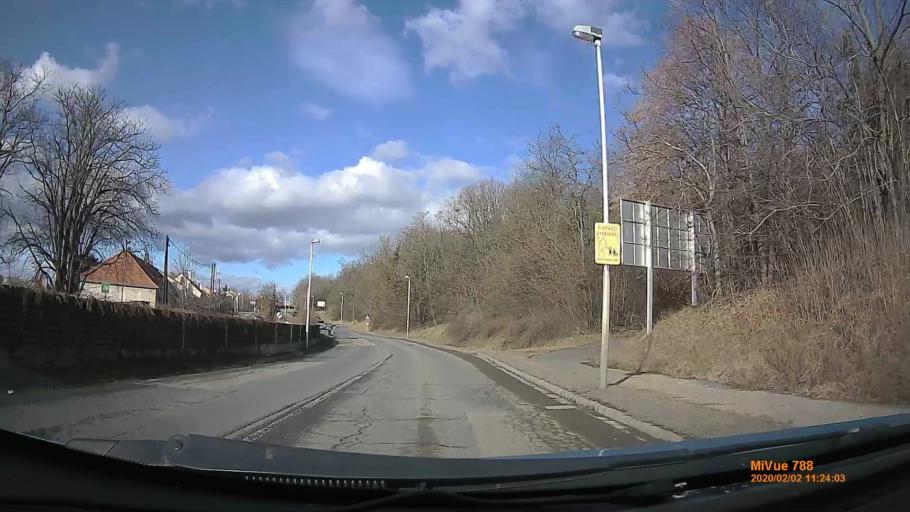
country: HU
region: Gyor-Moson-Sopron
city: Sopron
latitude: 47.6934
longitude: 16.5877
